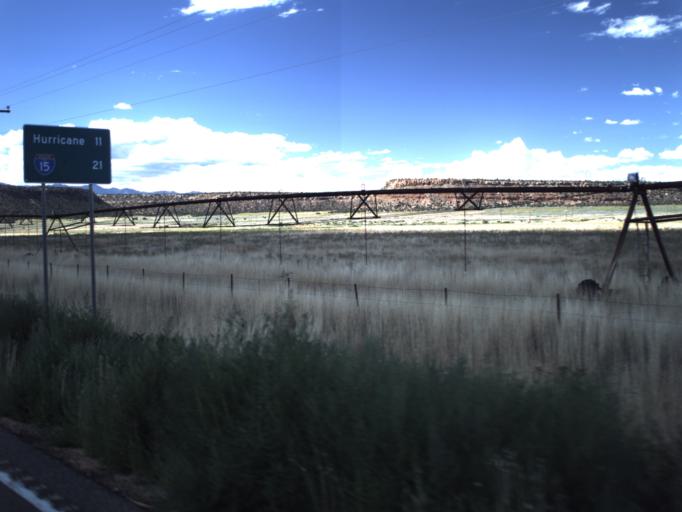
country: US
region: Utah
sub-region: Washington County
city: LaVerkin
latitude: 37.1052
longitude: -113.1373
